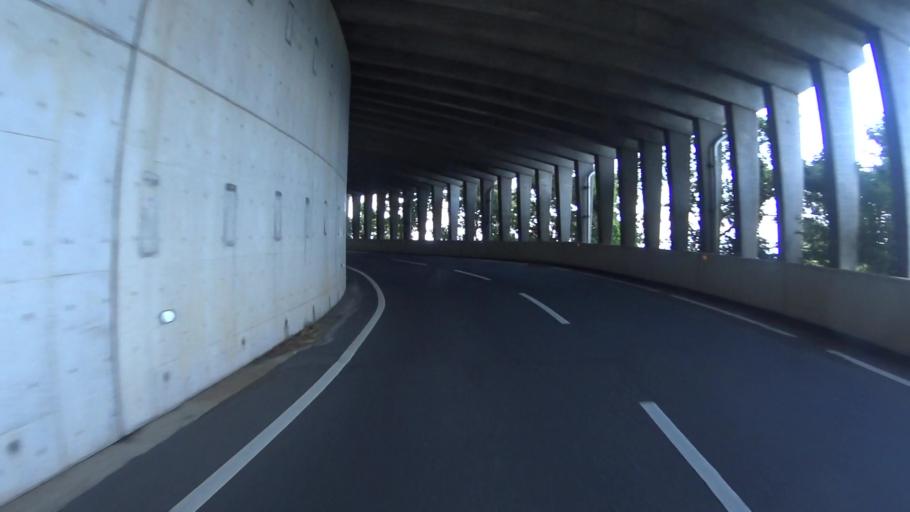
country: JP
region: Kyoto
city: Miyazu
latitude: 35.7617
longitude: 135.2395
